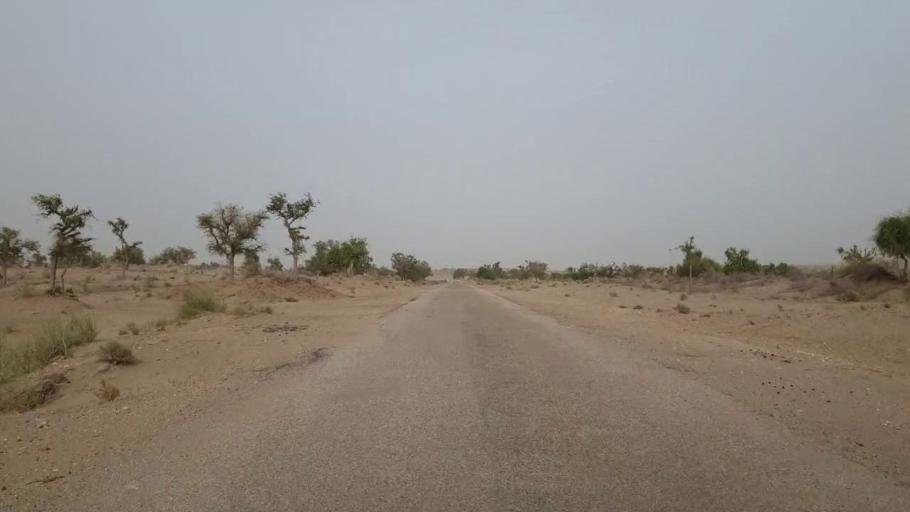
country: PK
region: Sindh
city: Islamkot
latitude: 24.5449
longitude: 70.3749
